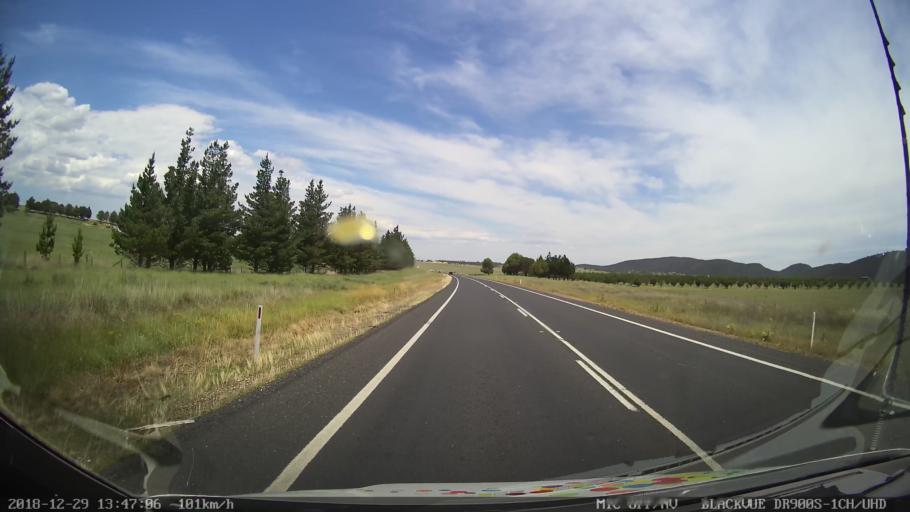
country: AU
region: New South Wales
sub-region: Cooma-Monaro
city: Cooma
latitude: -36.1214
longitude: 149.1425
